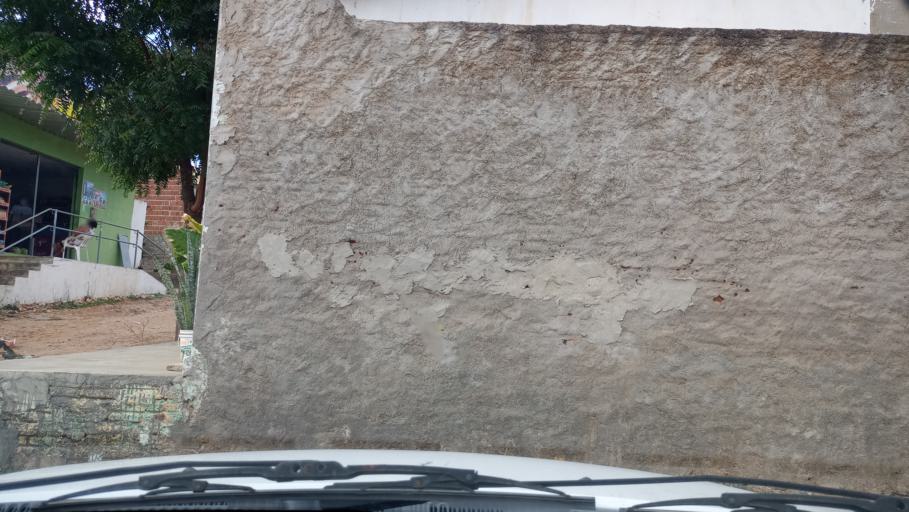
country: BR
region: Rio Grande do Norte
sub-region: Sao Tome
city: Sao Tome
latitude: -5.9437
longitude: -35.9264
